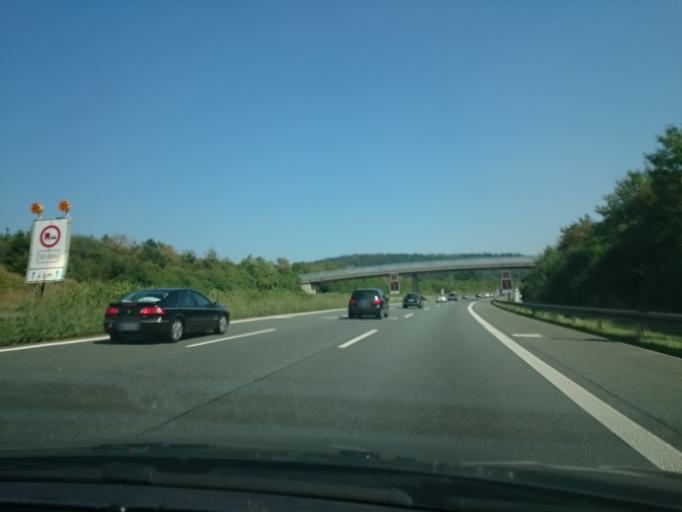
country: DE
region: Bavaria
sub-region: Upper Franconia
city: Himmelkron
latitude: 50.0626
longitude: 11.6188
